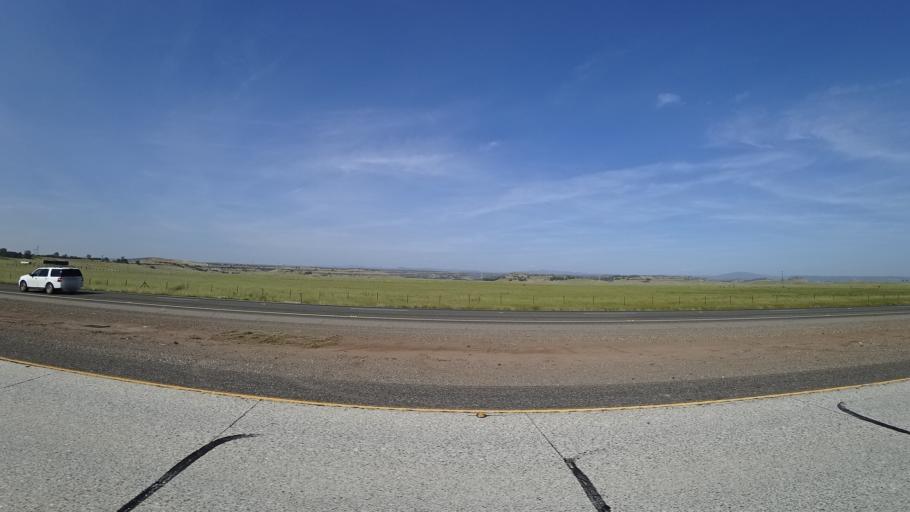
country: US
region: California
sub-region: Butte County
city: Durham
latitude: 39.6541
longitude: -121.7299
